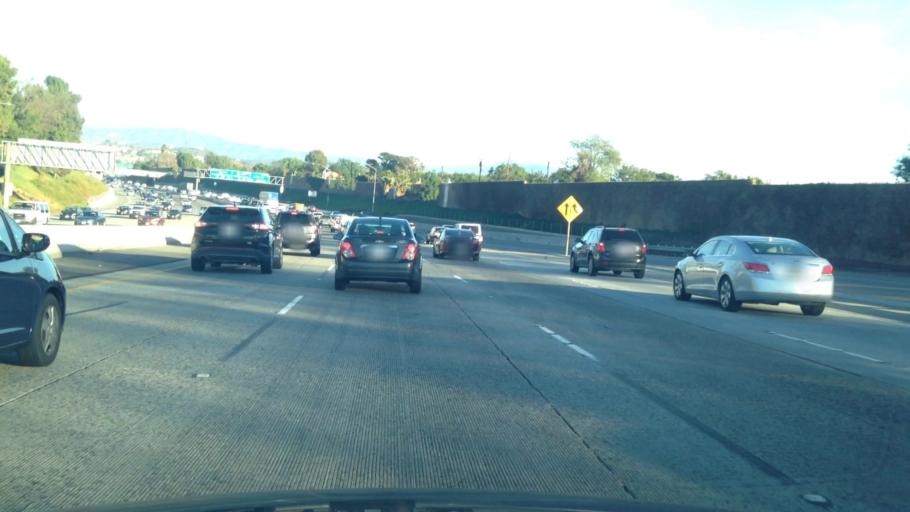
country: US
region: California
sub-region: Orange County
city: Orange
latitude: 33.7752
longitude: -117.8508
